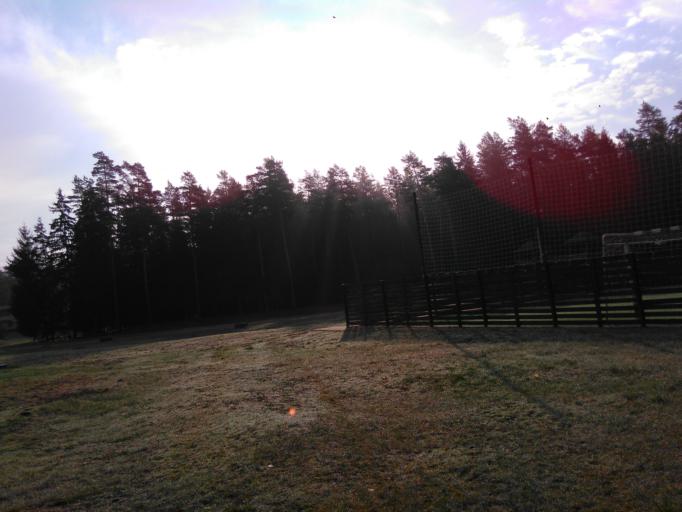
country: BY
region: Minsk
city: Rakaw
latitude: 53.9691
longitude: 27.0150
